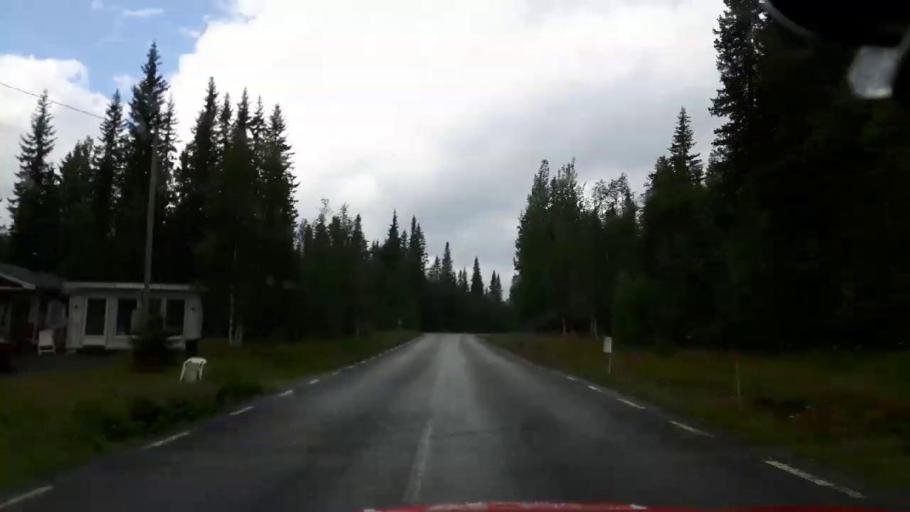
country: SE
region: Vaesterbotten
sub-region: Vilhelmina Kommun
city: Sjoberg
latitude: 64.9421
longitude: 15.7615
